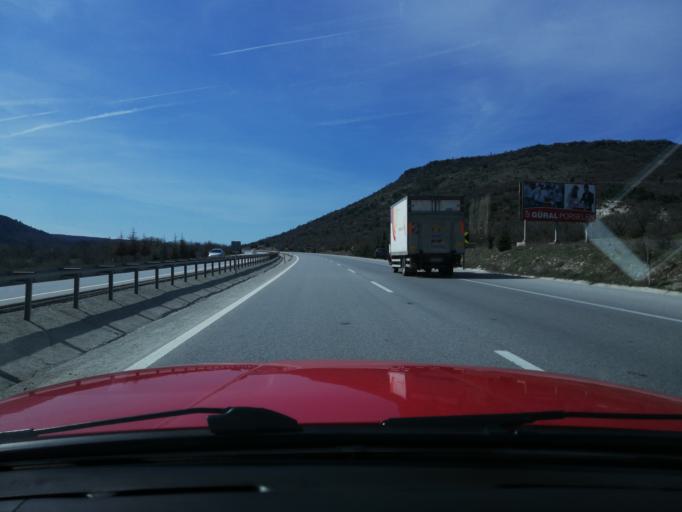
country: TR
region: Kuetahya
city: Sabuncu
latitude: 39.6047
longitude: 30.1474
